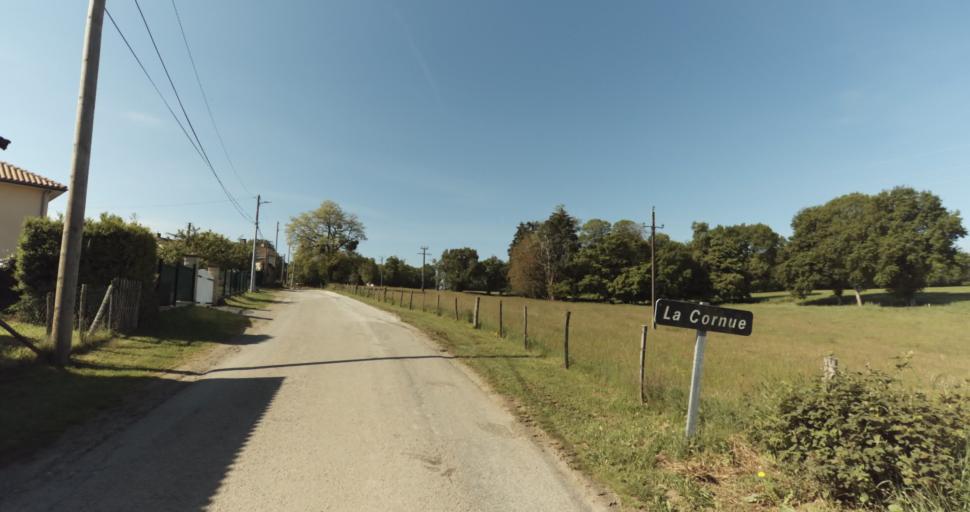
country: FR
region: Limousin
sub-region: Departement de la Haute-Vienne
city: Solignac
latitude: 45.7207
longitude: 1.2677
